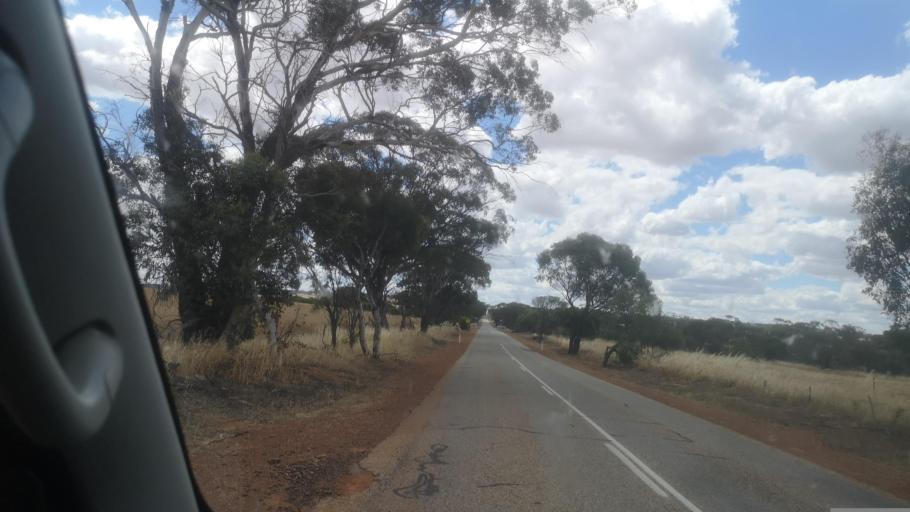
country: AU
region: Western Australia
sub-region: Beverley
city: Beverley
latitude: -31.9821
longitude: 117.0899
